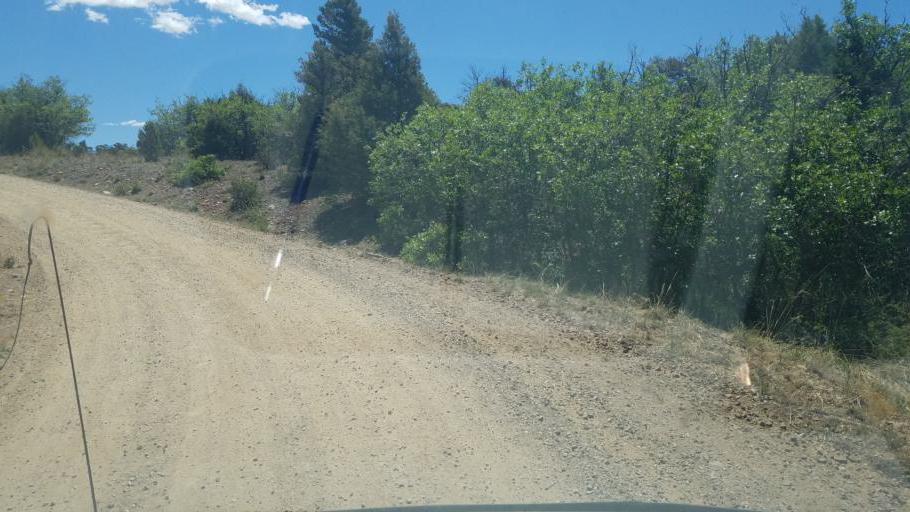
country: US
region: Colorado
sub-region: Custer County
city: Westcliffe
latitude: 38.3028
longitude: -105.6710
